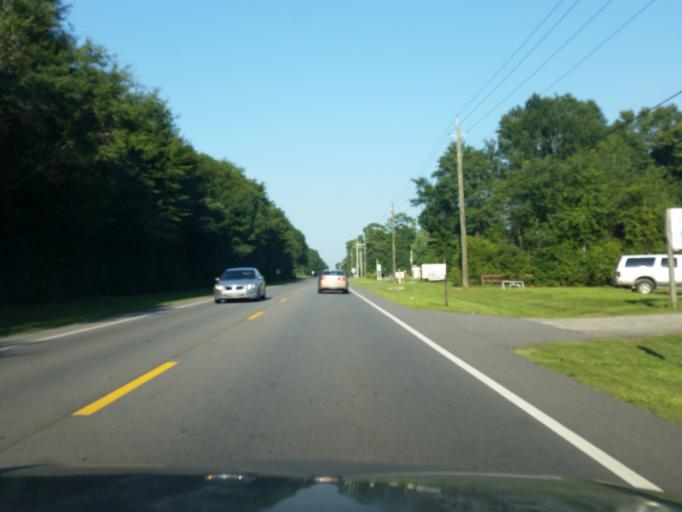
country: US
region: Alabama
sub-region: Baldwin County
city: Foley
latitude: 30.4068
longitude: -87.6649
